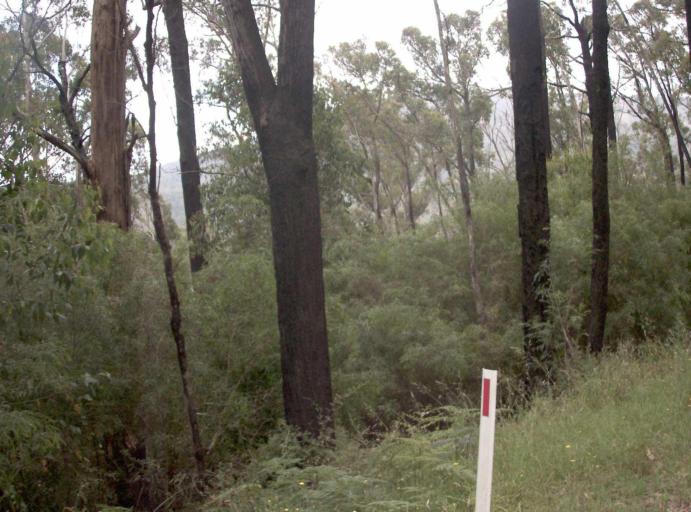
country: AU
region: Victoria
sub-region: Yarra Ranges
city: Healesville
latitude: -37.6409
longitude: 145.5784
